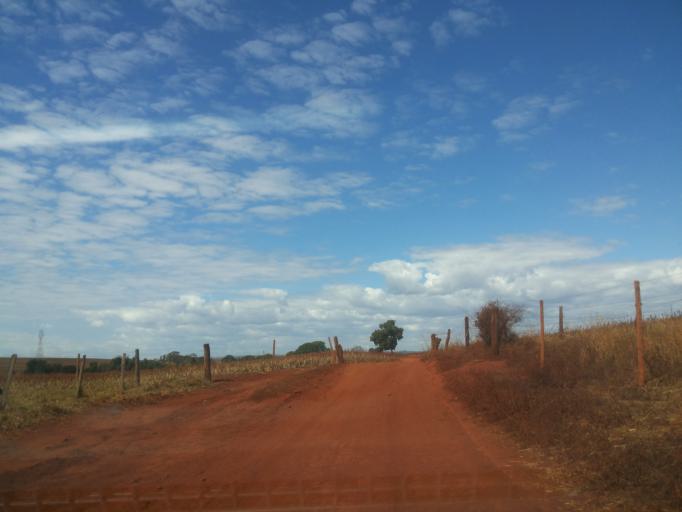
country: BR
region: Minas Gerais
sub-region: Centralina
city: Centralina
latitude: -18.5536
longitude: -49.2374
